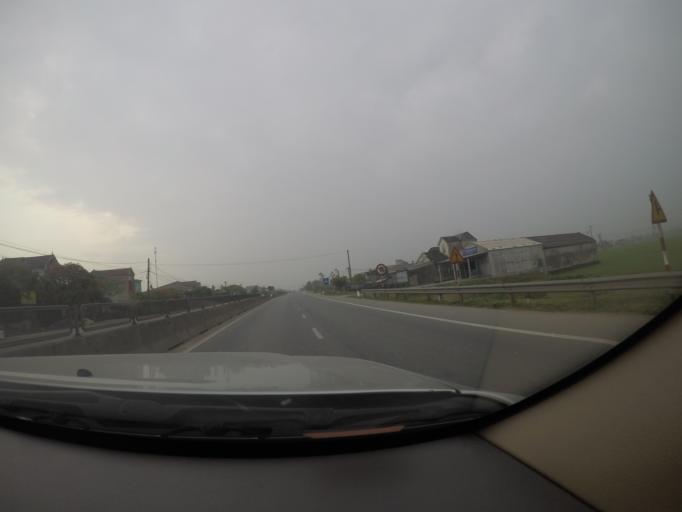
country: VN
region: Ha Tinh
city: Ky Anh
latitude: 18.1779
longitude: 106.2106
